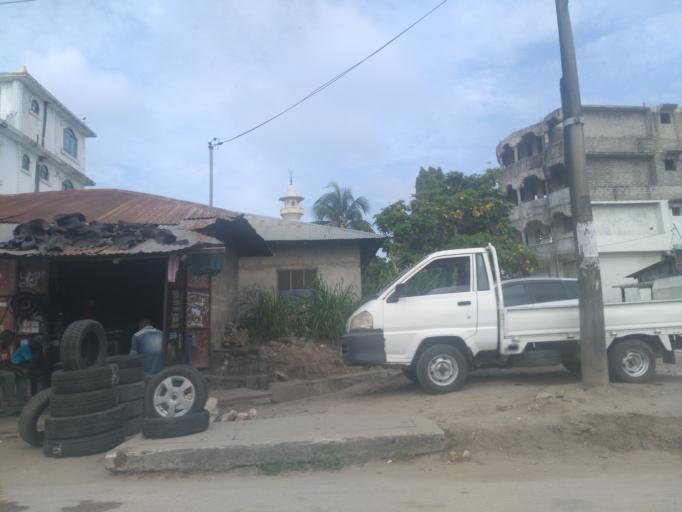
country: TZ
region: Zanzibar Urban/West
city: Zanzibar
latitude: -6.1667
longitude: 39.2030
